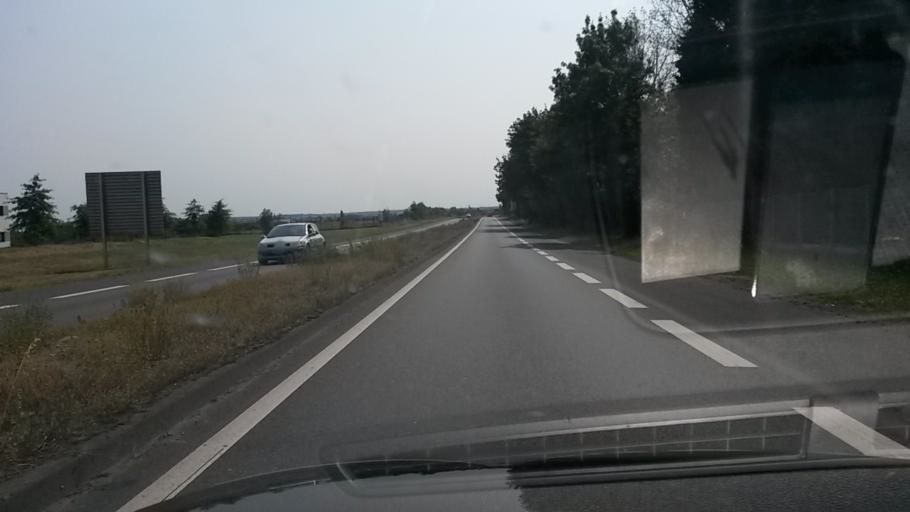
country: FR
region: Pays de la Loire
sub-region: Departement de la Loire-Atlantique
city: Saint-Gereon
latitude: 47.4084
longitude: -1.1899
